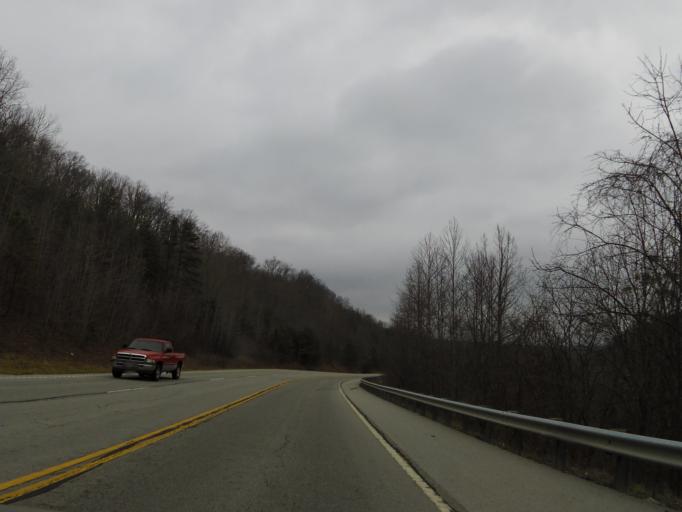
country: US
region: Tennessee
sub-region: Scott County
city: Huntsville
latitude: 36.3737
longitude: -84.5719
